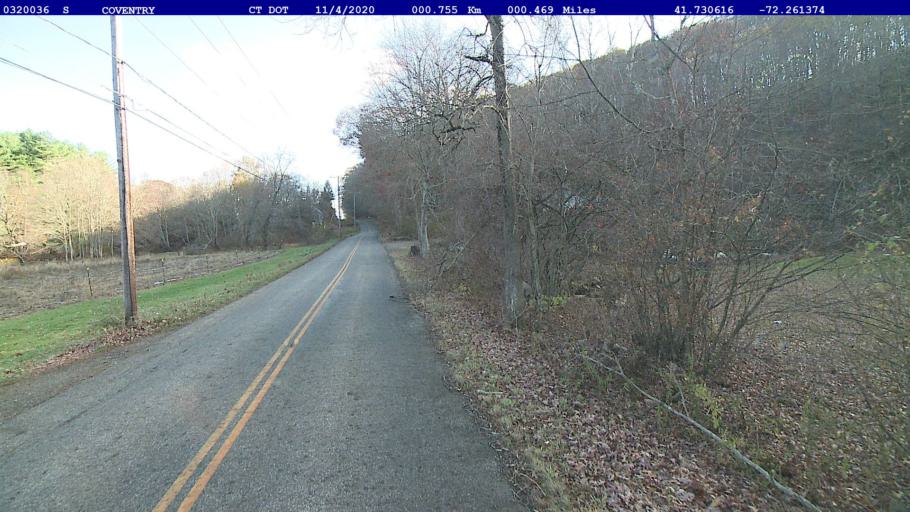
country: US
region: Connecticut
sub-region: Tolland County
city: Mansfield City
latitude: 41.7306
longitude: -72.2614
